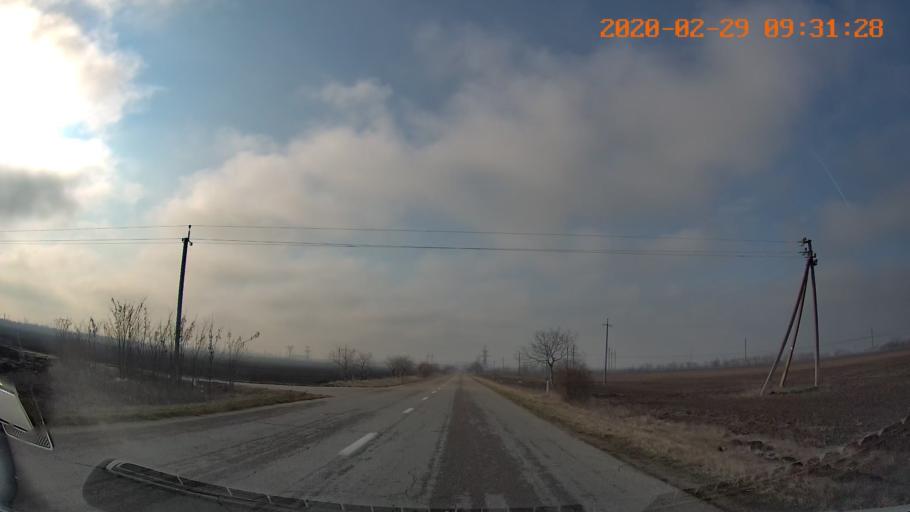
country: MD
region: Telenesti
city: Dnestrovsc
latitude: 46.6526
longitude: 29.9111
